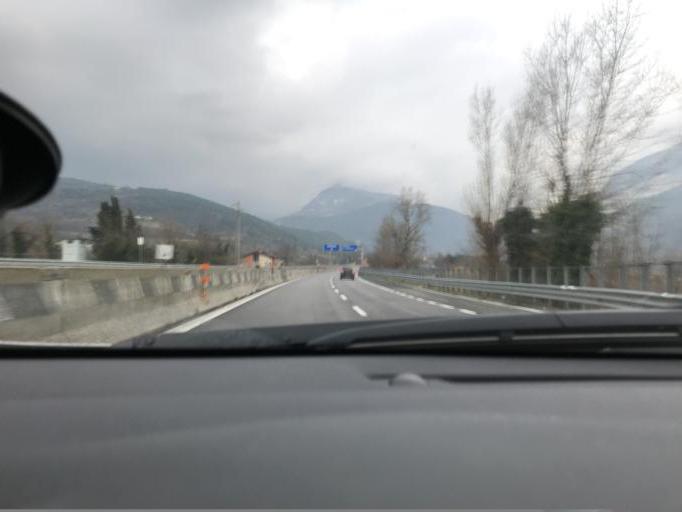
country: IT
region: The Marches
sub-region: Provincia di Ancona
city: Serra San Quirico
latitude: 43.4440
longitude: 13.0319
